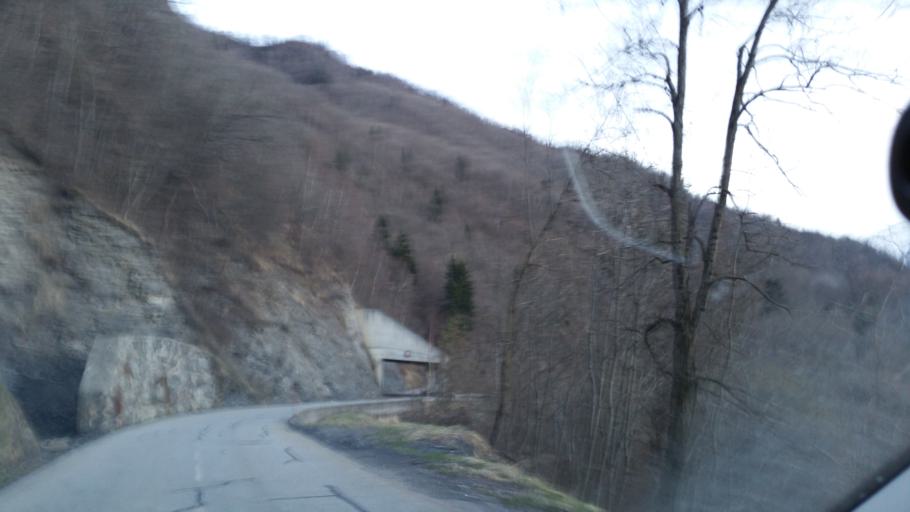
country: FR
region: Rhone-Alpes
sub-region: Departement de la Savoie
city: La Chambre
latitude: 45.3904
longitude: 6.3364
